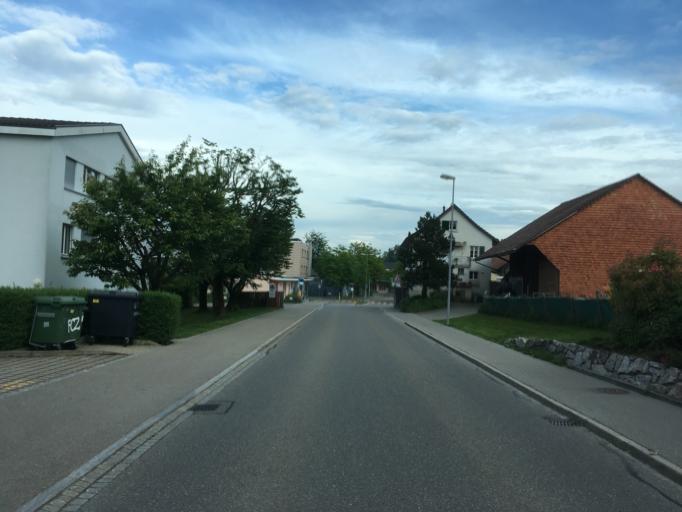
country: CH
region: Zurich
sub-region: Bezirk Uster
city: Binz
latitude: 47.3576
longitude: 8.6273
